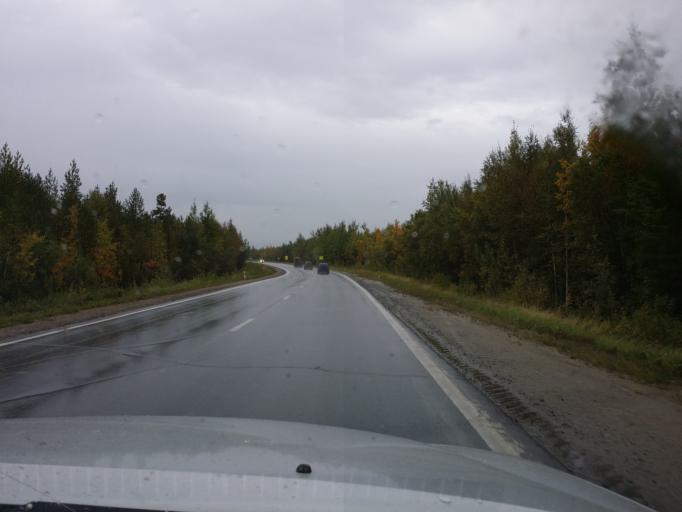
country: RU
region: Khanty-Mansiyskiy Avtonomnyy Okrug
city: Langepas
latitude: 61.1610
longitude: 75.5952
